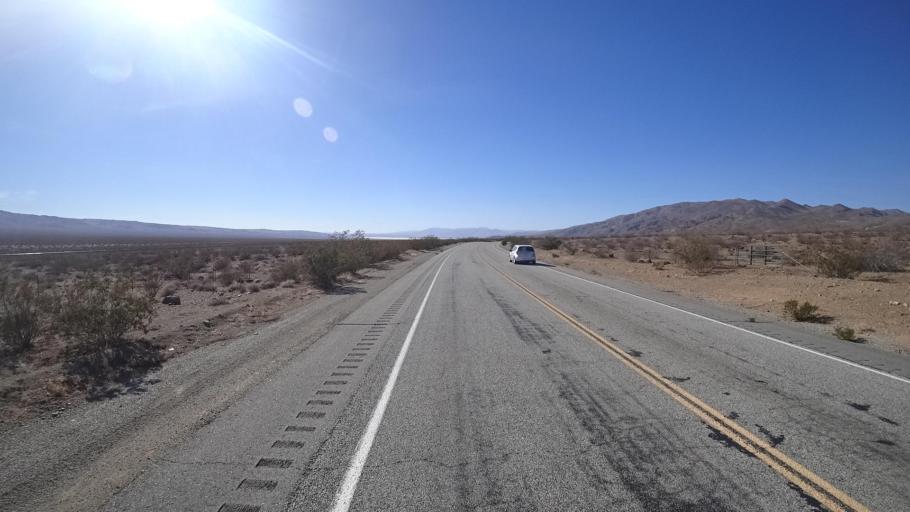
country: US
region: California
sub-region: Kern County
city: Ridgecrest
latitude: 35.4234
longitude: -117.7324
